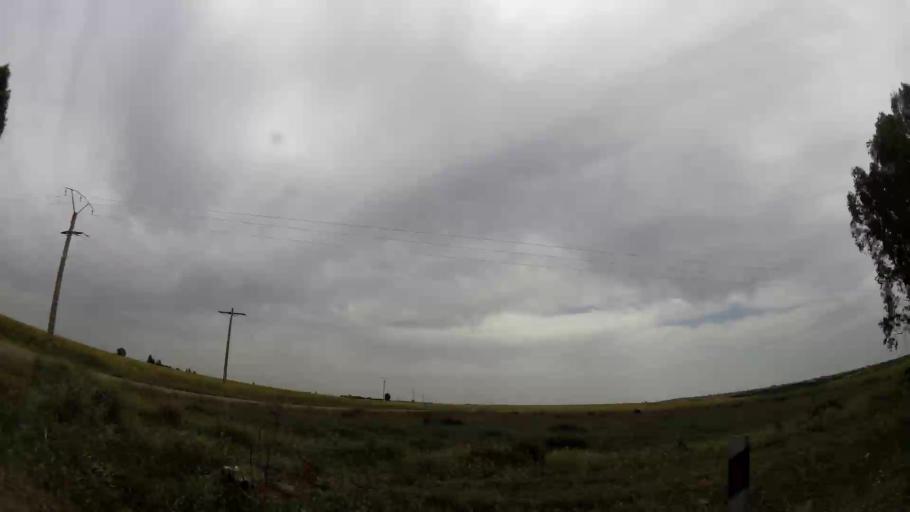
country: MA
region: Rabat-Sale-Zemmour-Zaer
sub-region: Khemisset
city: Tiflet
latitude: 33.8751
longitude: -6.2802
